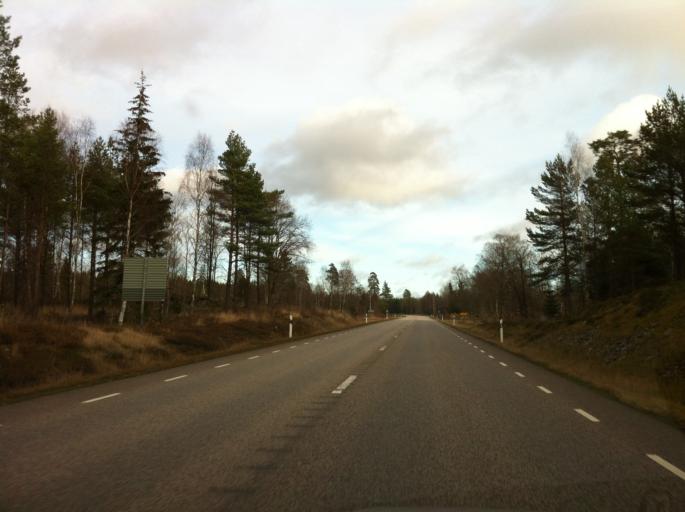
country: SE
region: Kronoberg
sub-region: Uppvidinge Kommun
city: Lenhovda
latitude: 57.1068
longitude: 15.2076
